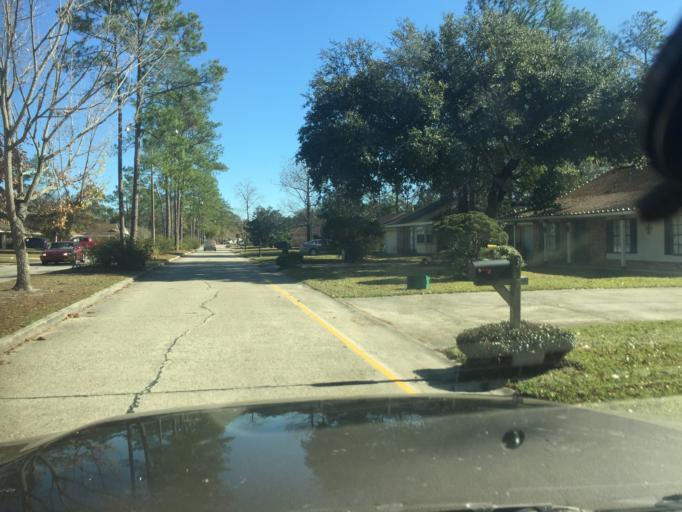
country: US
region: Louisiana
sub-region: Saint Tammany Parish
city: Slidell
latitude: 30.3003
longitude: -89.7375
